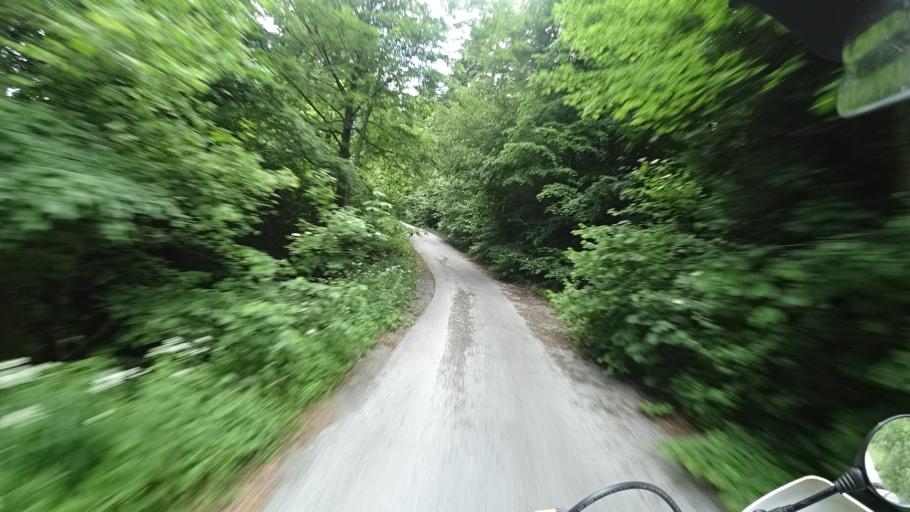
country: HR
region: Primorsko-Goranska
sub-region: Grad Crikvenica
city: Crikvenica
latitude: 45.2655
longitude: 14.7101
